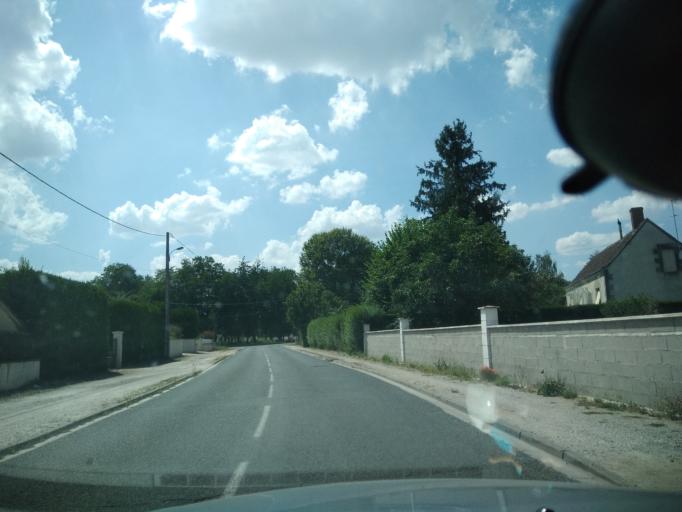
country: FR
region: Centre
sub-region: Departement d'Indre-et-Loire
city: Civray-de-Touraine
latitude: 47.3229
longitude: 1.0383
